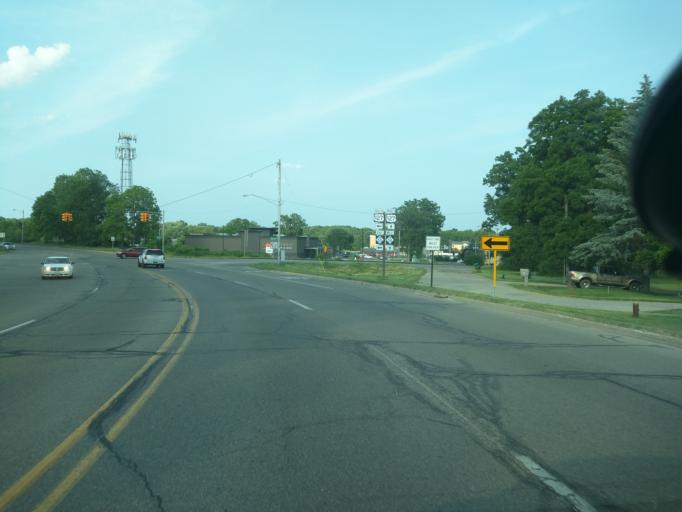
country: US
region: Michigan
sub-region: Jackson County
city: Jackson
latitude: 42.2766
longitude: -84.4345
